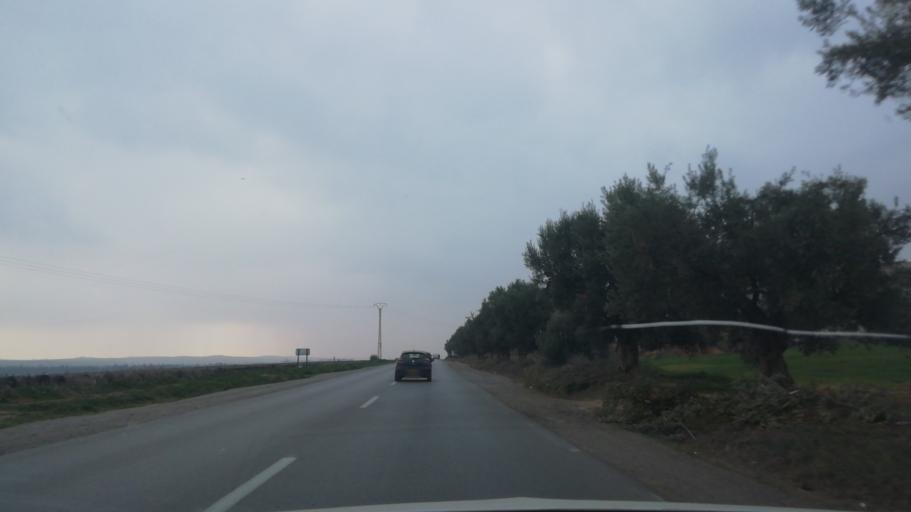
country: DZ
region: Sidi Bel Abbes
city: Sfizef
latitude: 35.2460
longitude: -0.2149
